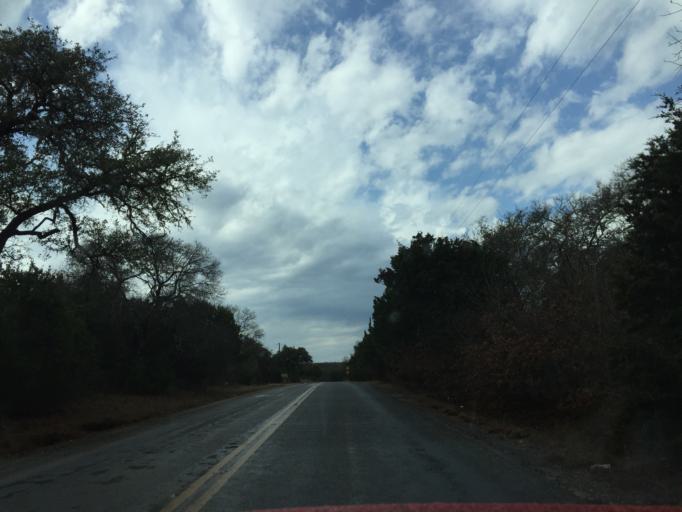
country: US
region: Texas
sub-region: Williamson County
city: Leander
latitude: 30.6307
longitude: -97.9740
